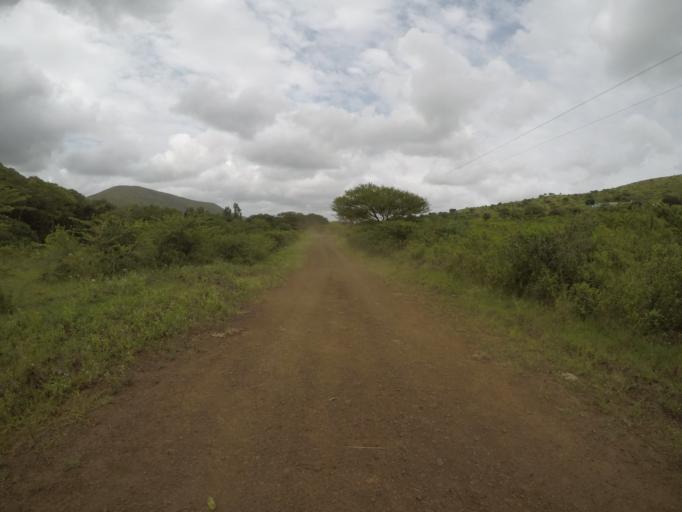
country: ZA
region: KwaZulu-Natal
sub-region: uThungulu District Municipality
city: Empangeni
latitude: -28.5840
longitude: 31.8893
